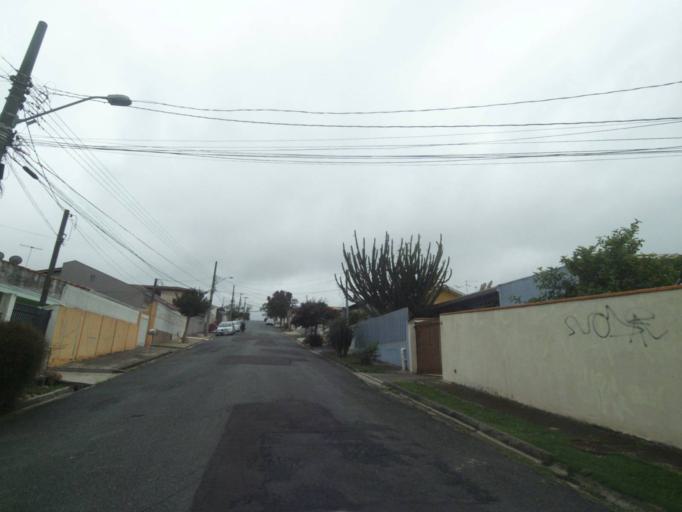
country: BR
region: Parana
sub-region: Curitiba
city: Curitiba
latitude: -25.4280
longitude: -49.3450
